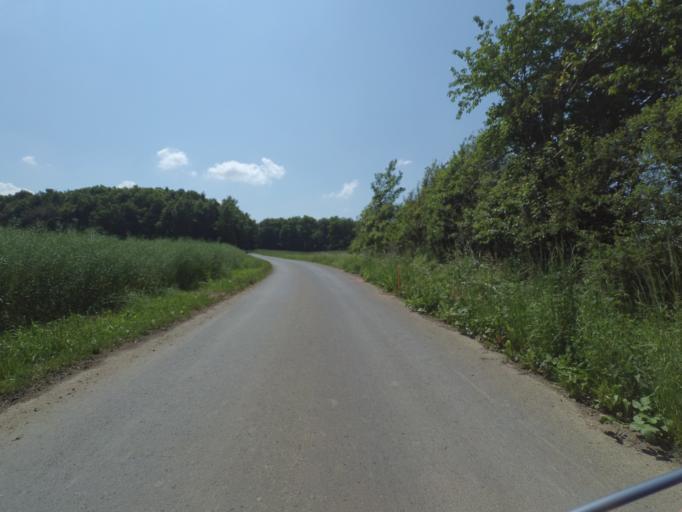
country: DE
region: Rheinland-Pfalz
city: Kalenborn
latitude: 50.2628
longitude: 7.0869
